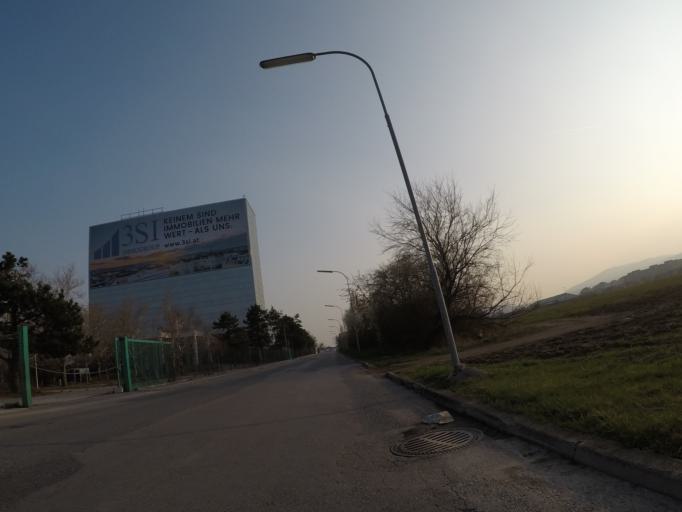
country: AT
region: Lower Austria
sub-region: Politischer Bezirk Modling
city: Wiener Neudorf
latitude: 48.0941
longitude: 16.3196
